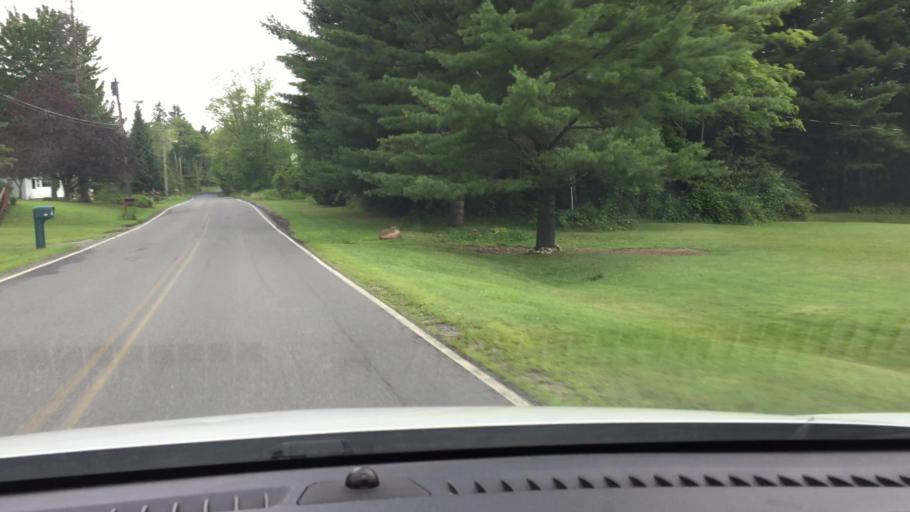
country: US
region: Massachusetts
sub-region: Berkshire County
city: Hinsdale
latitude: 42.4413
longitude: -73.1361
